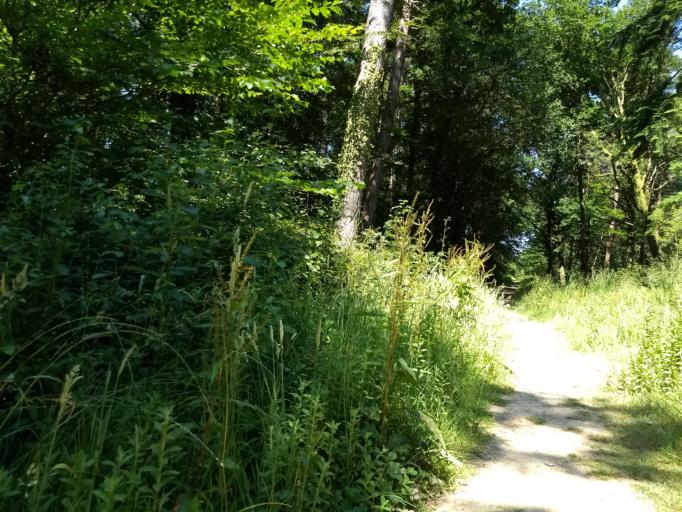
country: GB
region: England
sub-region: Isle of Wight
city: Northwood
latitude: 50.7071
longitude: -1.3342
